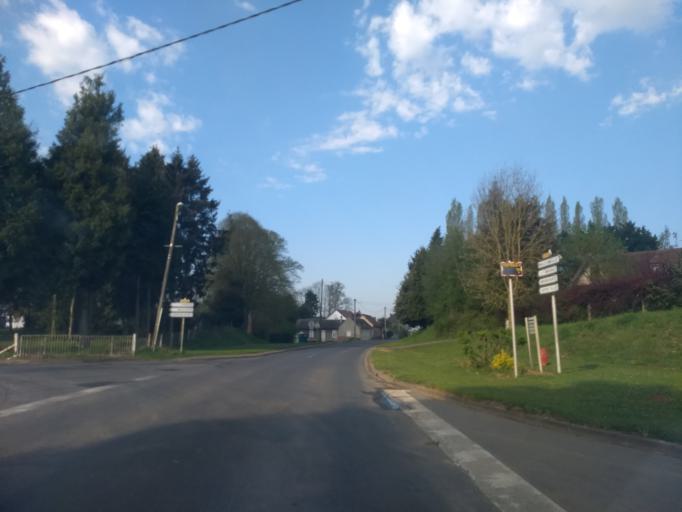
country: FR
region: Picardie
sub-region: Departement de la Somme
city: Corbie
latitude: 50.0122
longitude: 2.5266
